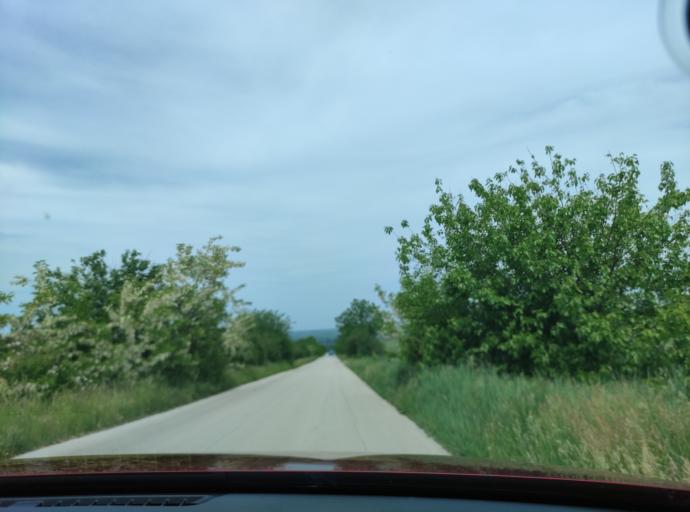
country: BG
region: Pleven
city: Iskur
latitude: 43.5288
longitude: 24.3097
